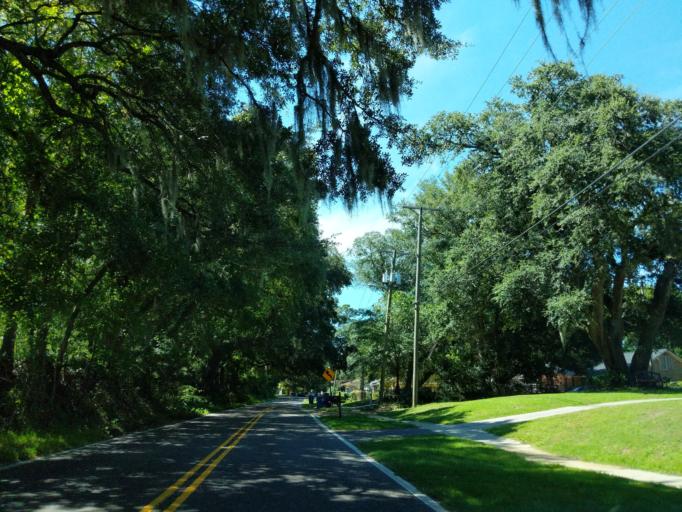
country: US
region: South Carolina
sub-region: Charleston County
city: Charleston
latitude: 32.7182
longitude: -79.9570
